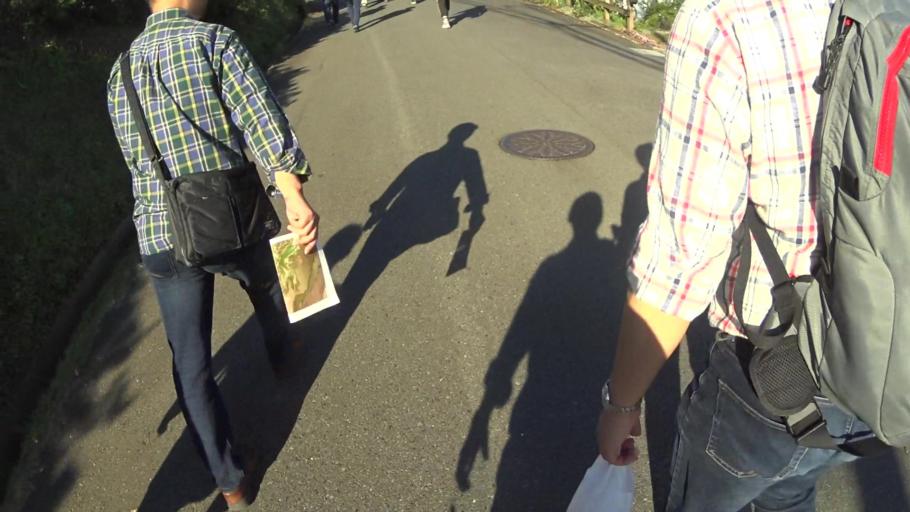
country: JP
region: Tokyo
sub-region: Machida-shi
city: Machida
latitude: 35.5776
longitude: 139.4444
